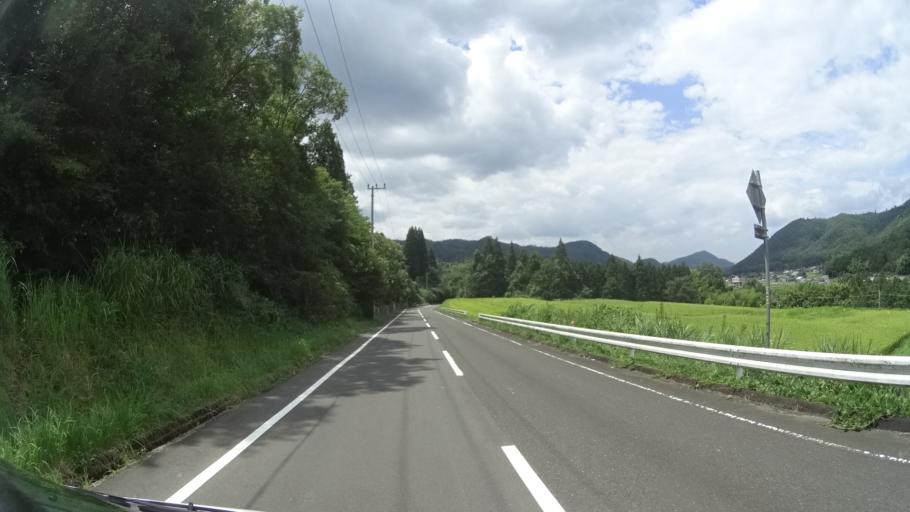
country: JP
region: Kyoto
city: Ayabe
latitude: 35.2870
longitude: 135.2973
